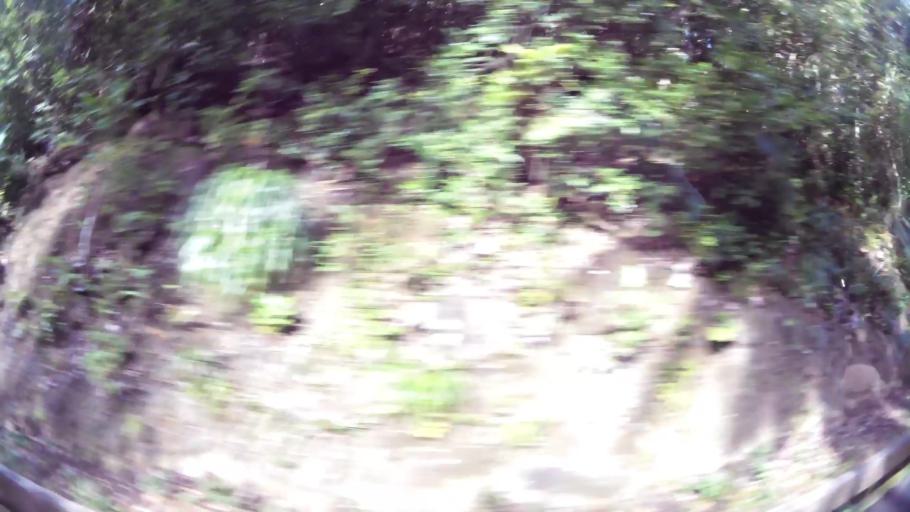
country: DM
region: Saint Andrew
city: Calibishie
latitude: 15.5951
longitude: -61.3632
